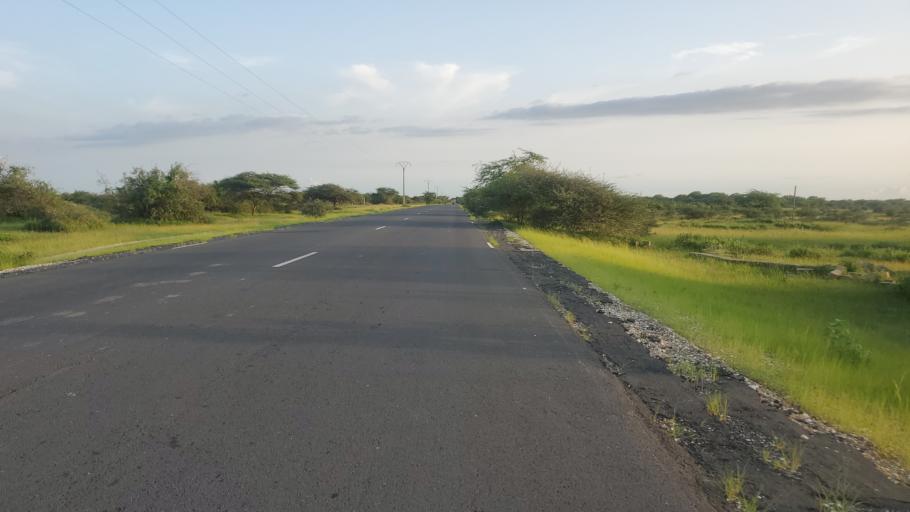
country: SN
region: Saint-Louis
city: Saint-Louis
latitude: 16.1773
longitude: -16.4096
